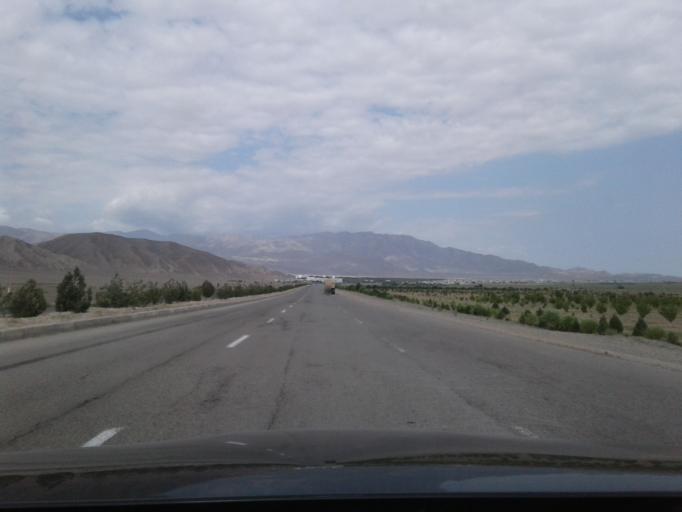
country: TM
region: Ahal
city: Baharly
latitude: 38.5131
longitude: 57.2254
